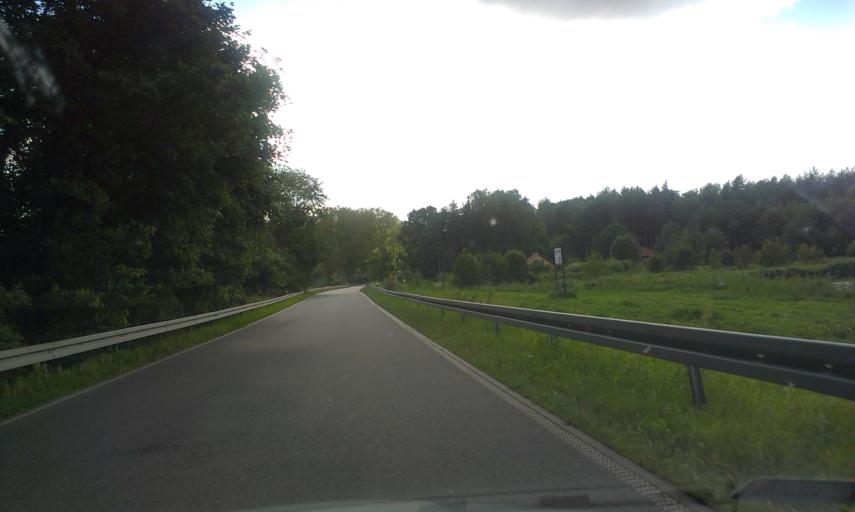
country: PL
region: Masovian Voivodeship
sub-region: Powiat zyrardowski
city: Radziejowice
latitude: 51.9669
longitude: 20.6127
